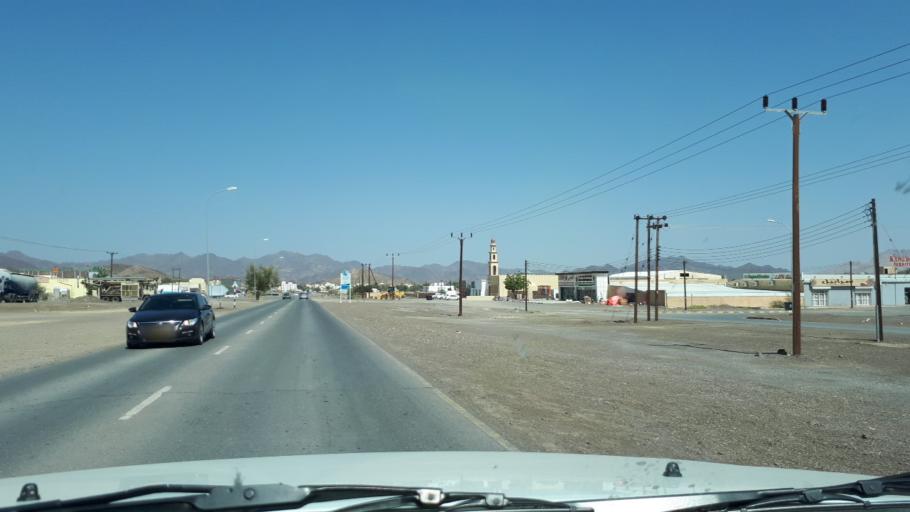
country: OM
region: Muhafazat ad Dakhiliyah
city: Bahla'
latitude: 22.9473
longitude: 57.2727
